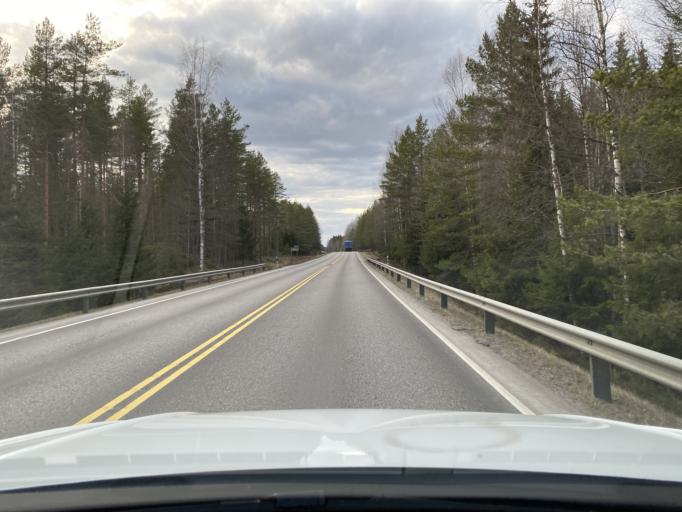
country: FI
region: Haeme
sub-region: Haemeenlinna
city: Renko
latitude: 60.8001
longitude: 24.0834
